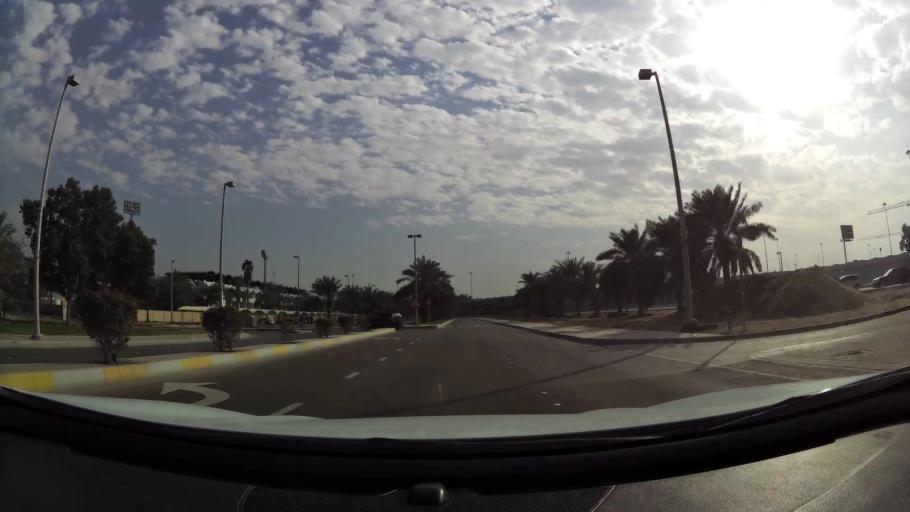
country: AE
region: Abu Dhabi
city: Abu Dhabi
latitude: 24.4083
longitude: 54.4796
